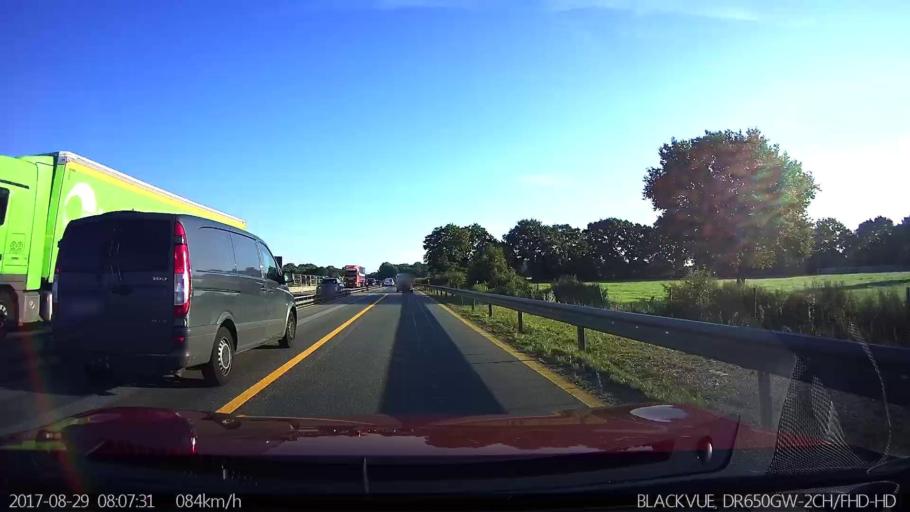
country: DE
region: Schleswig-Holstein
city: Bonningstedt
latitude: 53.6788
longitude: 9.9443
